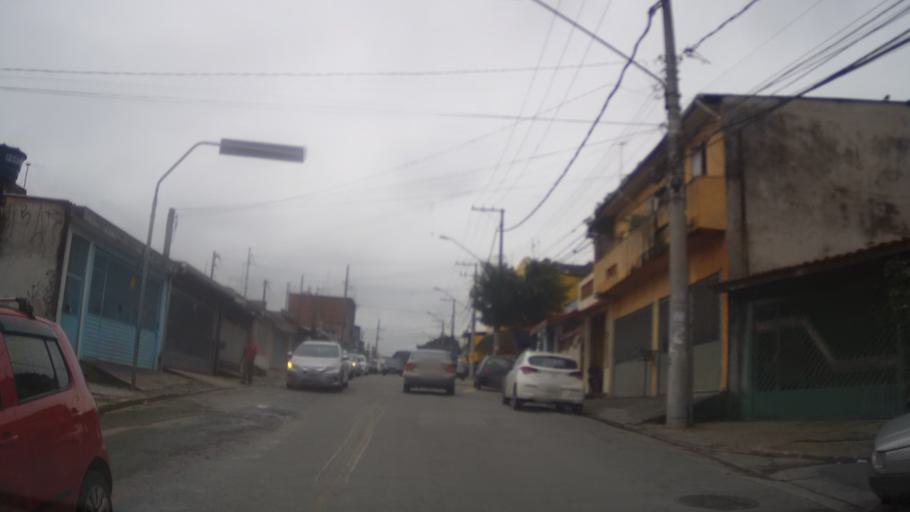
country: BR
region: Sao Paulo
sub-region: Guarulhos
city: Guarulhos
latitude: -23.4406
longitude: -46.5133
